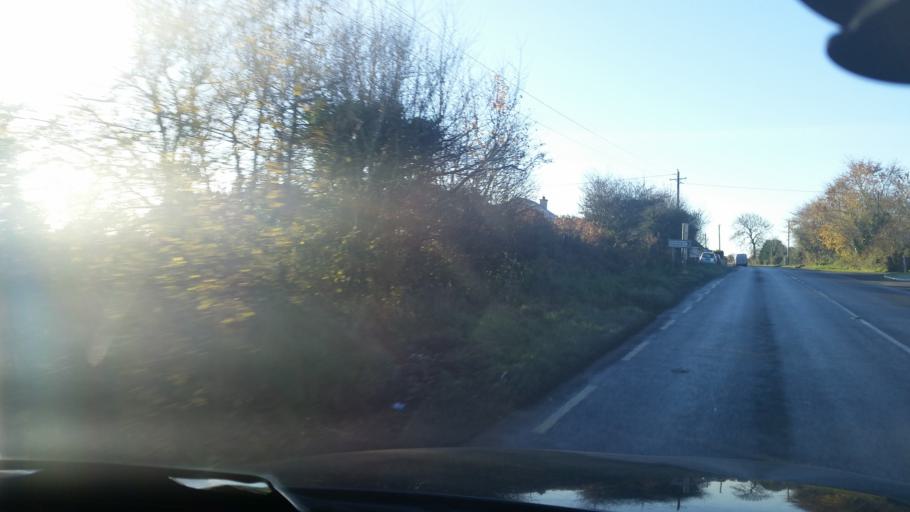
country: IE
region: Leinster
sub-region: Loch Garman
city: Ballinroad
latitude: 52.5613
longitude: -6.3349
